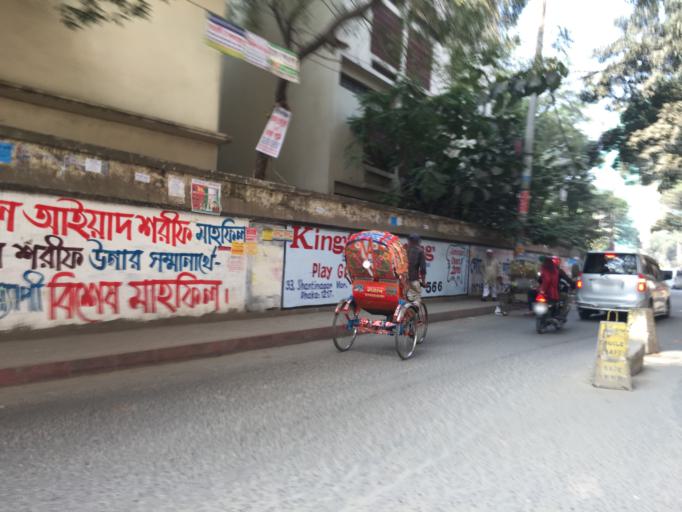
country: BD
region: Dhaka
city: Paltan
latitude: 23.7429
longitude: 90.4076
